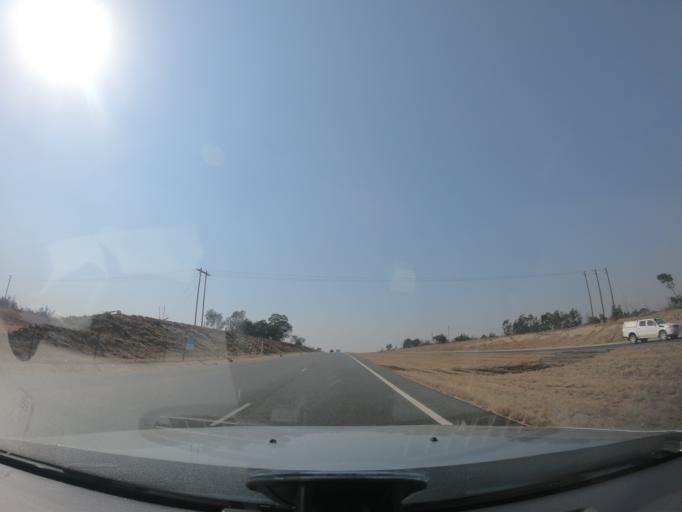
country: ZA
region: Mpumalanga
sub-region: Nkangala District Municipality
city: Witbank
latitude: -25.8696
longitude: 29.0589
